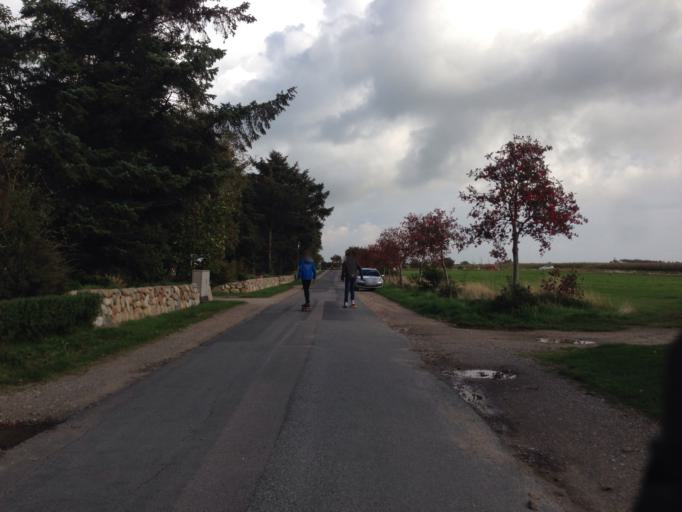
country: DE
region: Schleswig-Holstein
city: Utersum
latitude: 54.7081
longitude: 8.4030
